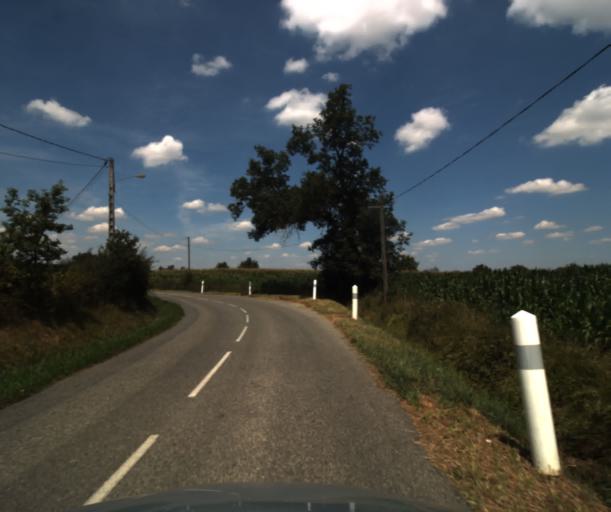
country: FR
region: Midi-Pyrenees
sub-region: Departement de la Haute-Garonne
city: Saint-Lys
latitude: 43.4910
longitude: 1.1806
